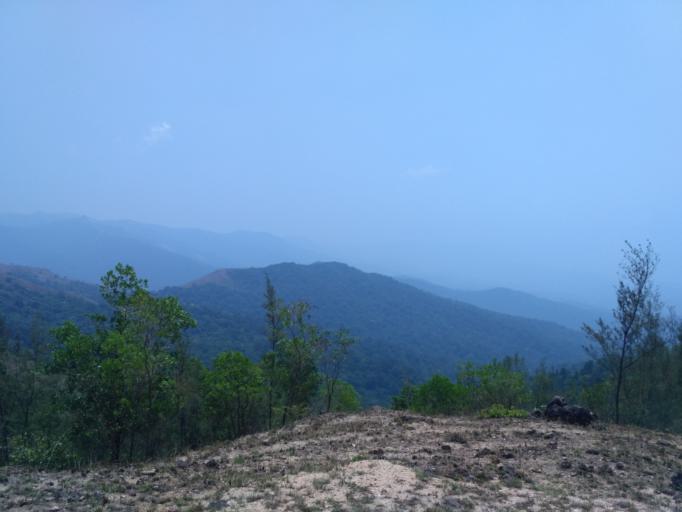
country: IN
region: Karnataka
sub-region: Kodagu
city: Somvarpet
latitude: 12.6684
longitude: 75.6505
